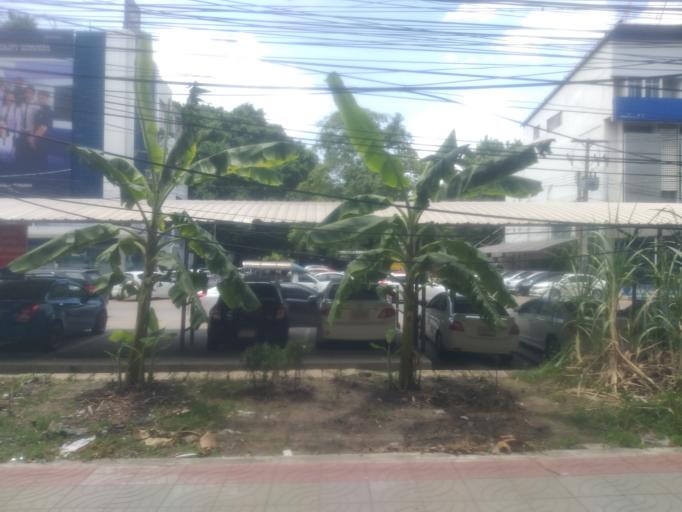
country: TH
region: Bangkok
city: Sai Mai
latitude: 13.9645
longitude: 100.6202
